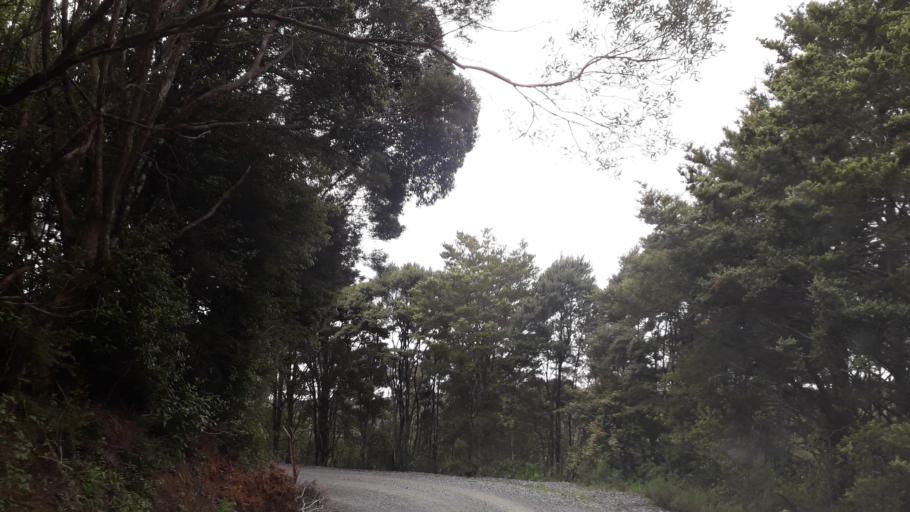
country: NZ
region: Northland
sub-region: Far North District
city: Taipa
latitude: -35.0860
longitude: 173.5525
